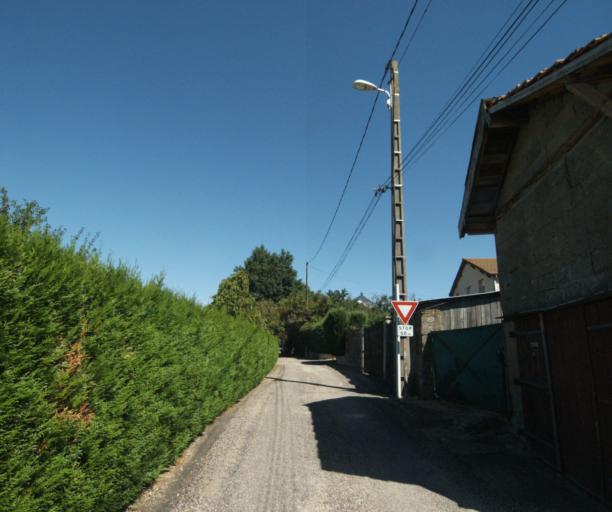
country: FR
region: Lorraine
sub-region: Departement des Vosges
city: Epinal
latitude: 48.1834
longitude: 6.4682
